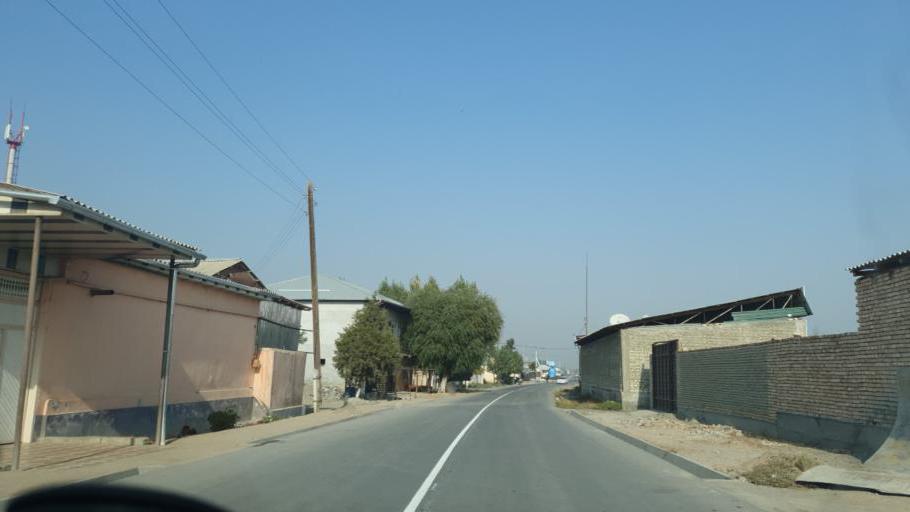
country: UZ
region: Fergana
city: Qo`qon
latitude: 40.5866
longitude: 70.9058
